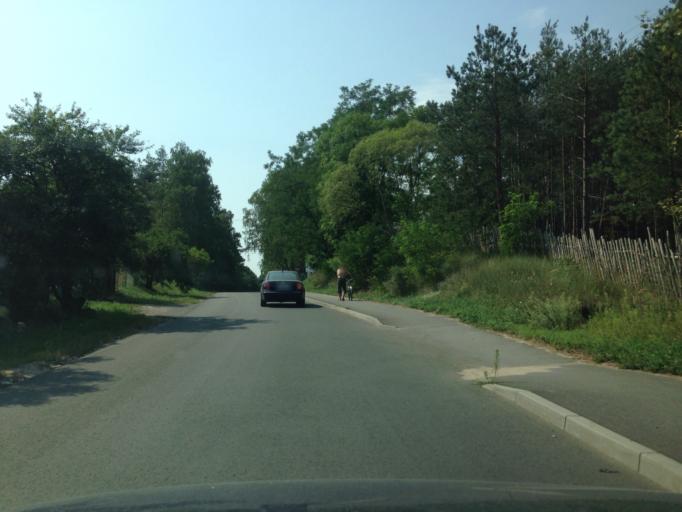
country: PL
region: Kujawsko-Pomorskie
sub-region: Powiat golubsko-dobrzynski
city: Golub-Dobrzyn
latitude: 53.0944
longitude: 19.0405
